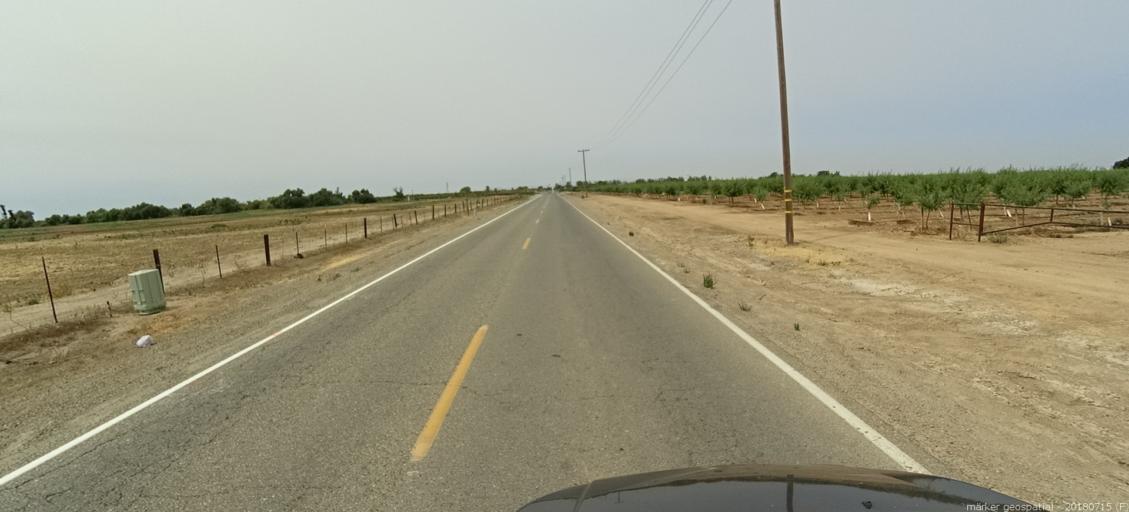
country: US
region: California
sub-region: Madera County
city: Madera Acres
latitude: 37.0145
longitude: -120.1105
